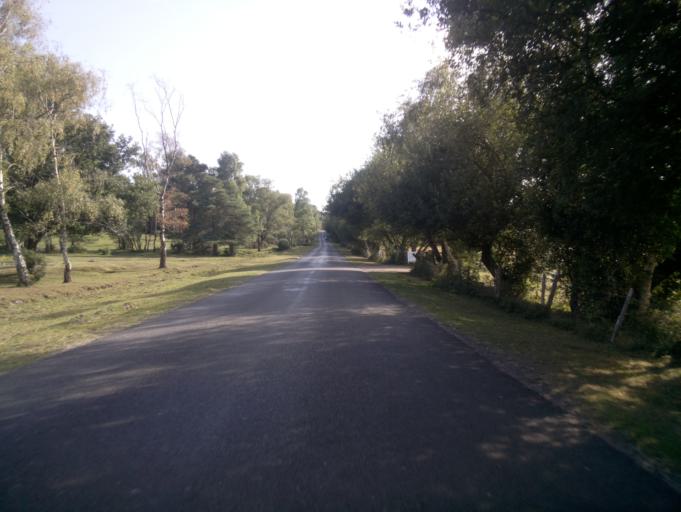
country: GB
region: England
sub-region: Hampshire
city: West Wellow
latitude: 50.9543
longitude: -1.5831
